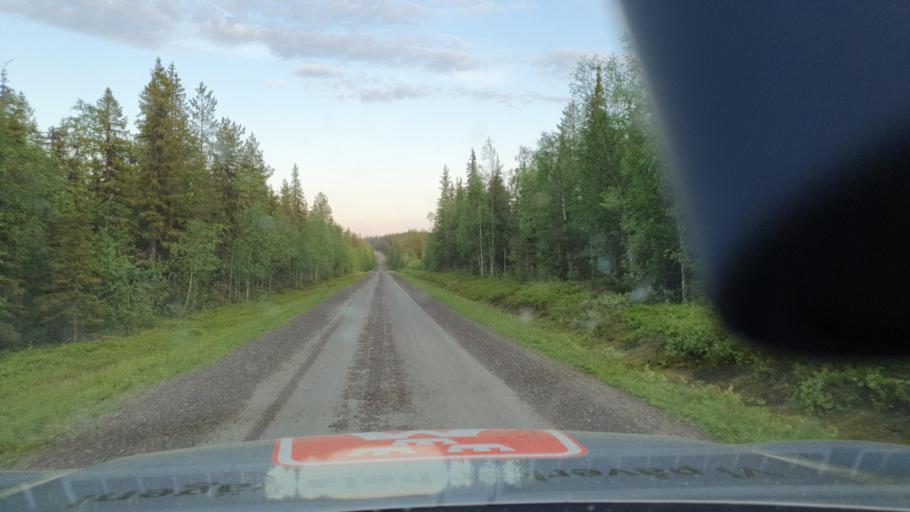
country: SE
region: Norrbotten
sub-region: Bodens Kommun
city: Boden
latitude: 66.4606
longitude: 21.6439
